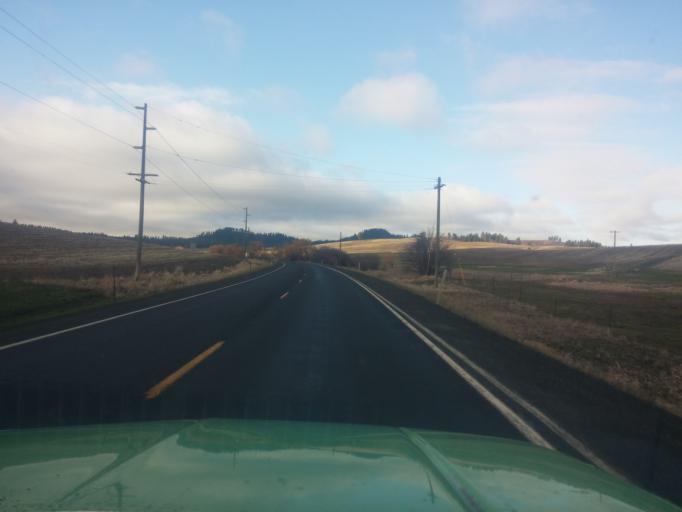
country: US
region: Idaho
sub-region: Latah County
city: Moscow
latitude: 46.8994
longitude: -116.9855
